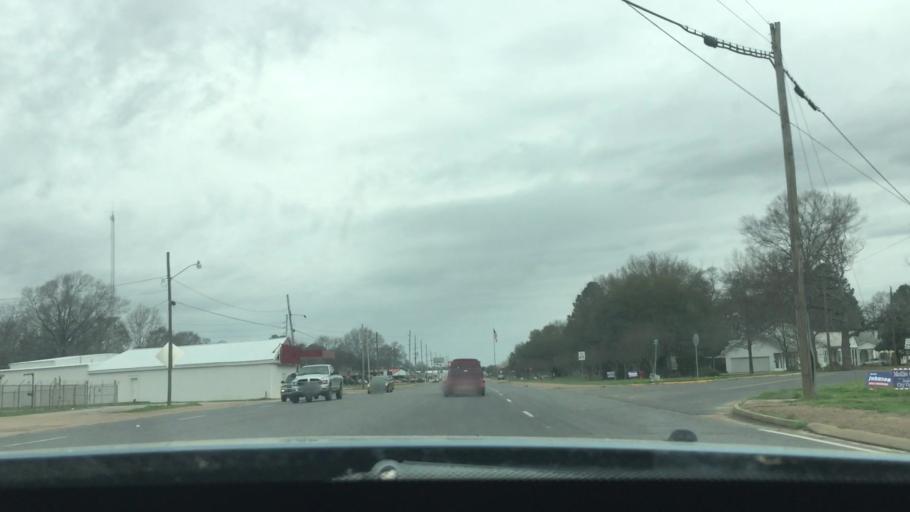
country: US
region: Louisiana
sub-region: Franklin Parish
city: Winnsboro
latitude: 32.1573
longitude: -91.7155
